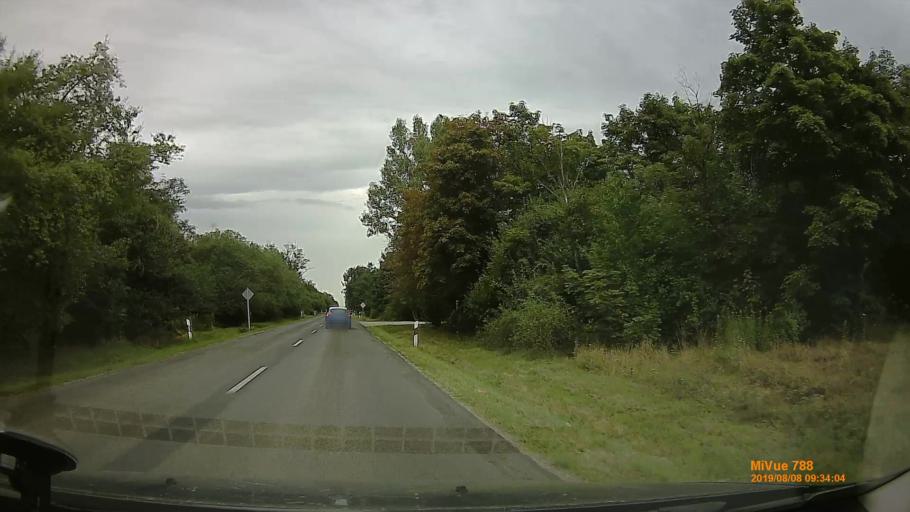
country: HU
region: Vas
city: Vasvar
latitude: 47.0295
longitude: 16.8150
